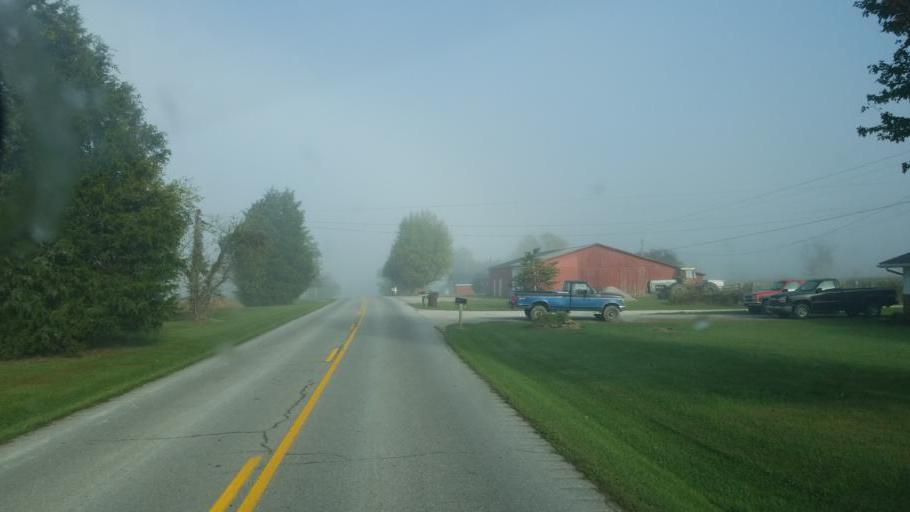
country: US
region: Kentucky
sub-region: Fleming County
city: Flemingsburg
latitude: 38.4839
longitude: -83.6104
